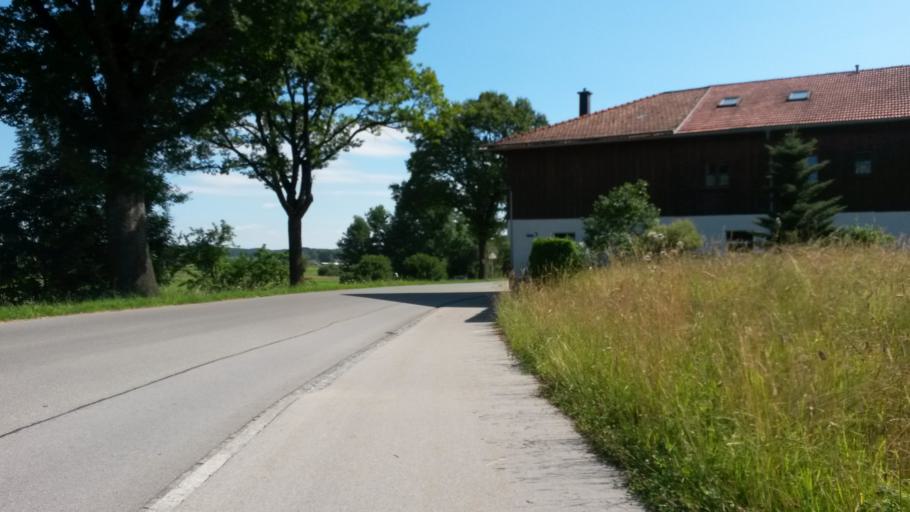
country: DE
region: Bavaria
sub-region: Upper Bavaria
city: Grabenstatt
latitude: 47.8354
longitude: 12.5321
